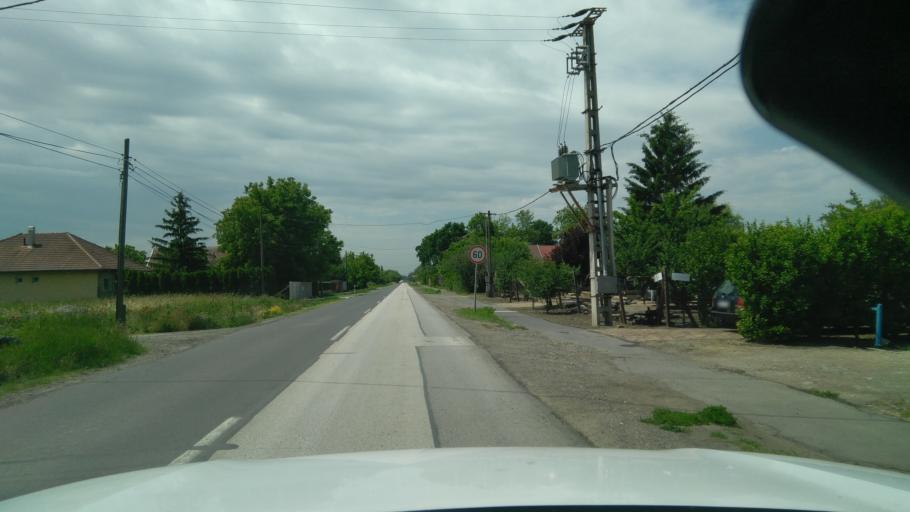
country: HU
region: Bekes
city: Bekescsaba
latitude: 46.6989
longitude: 21.1399
